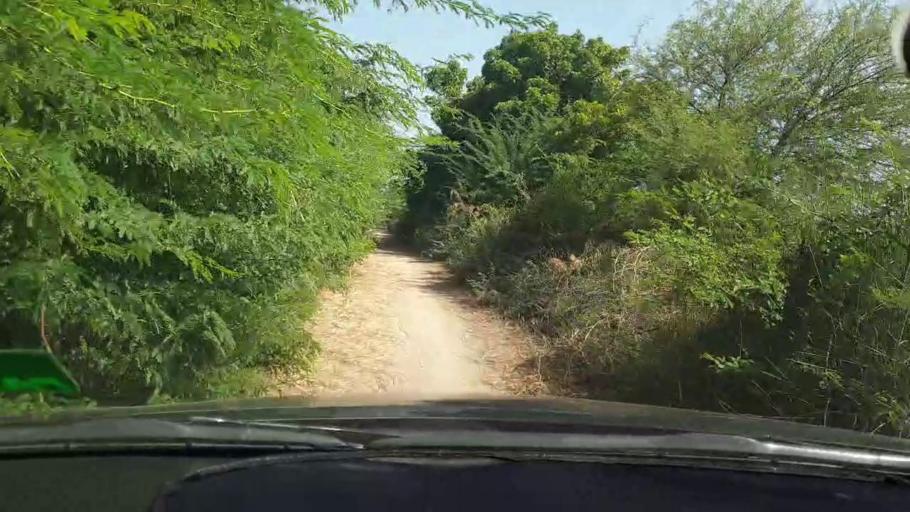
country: PK
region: Sindh
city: Tando Bago
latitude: 24.7741
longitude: 68.9456
